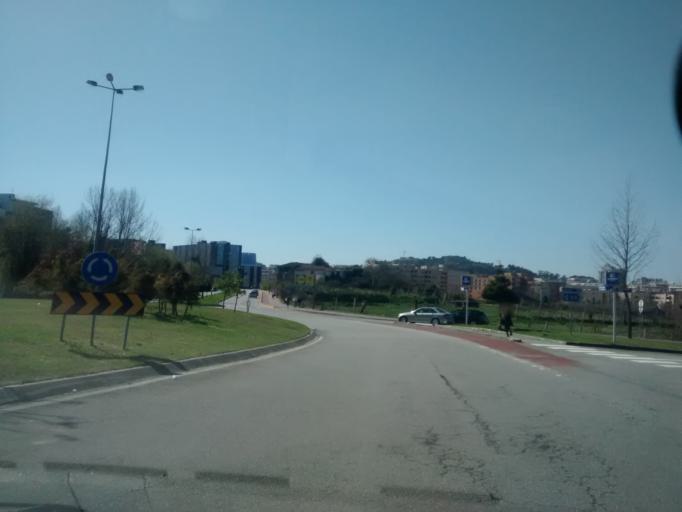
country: PT
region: Braga
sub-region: Braga
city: Braga
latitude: 41.5473
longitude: -8.3973
